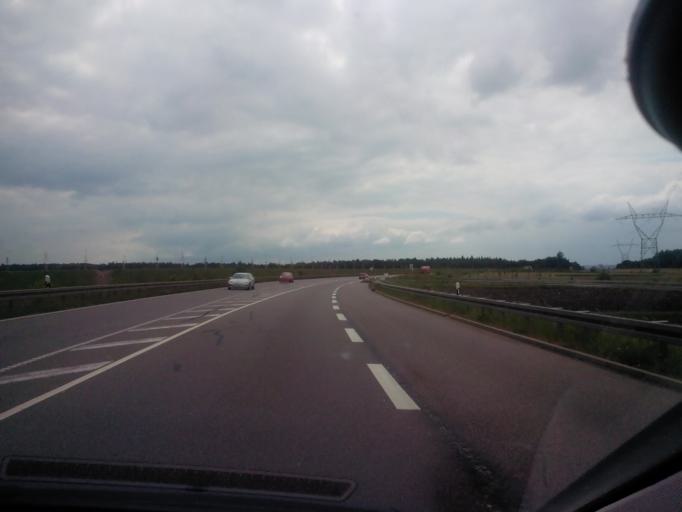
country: DE
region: Saarland
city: Wadgassen
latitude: 49.2751
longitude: 6.7506
